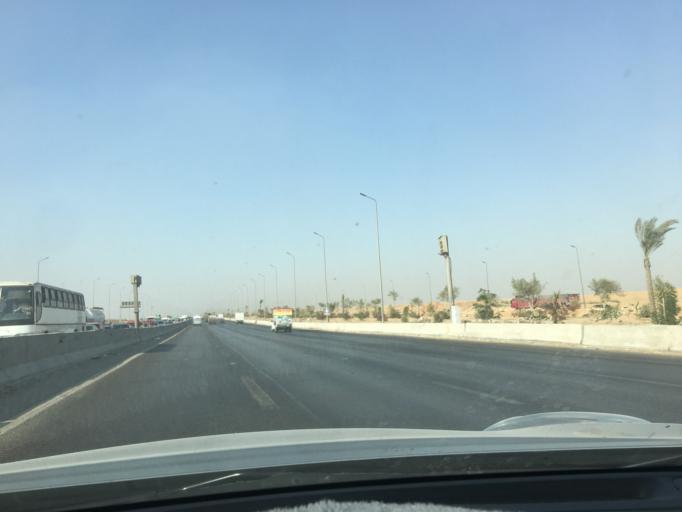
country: EG
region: Muhafazat al Qalyubiyah
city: Al Khankah
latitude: 30.0998
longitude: 31.4470
